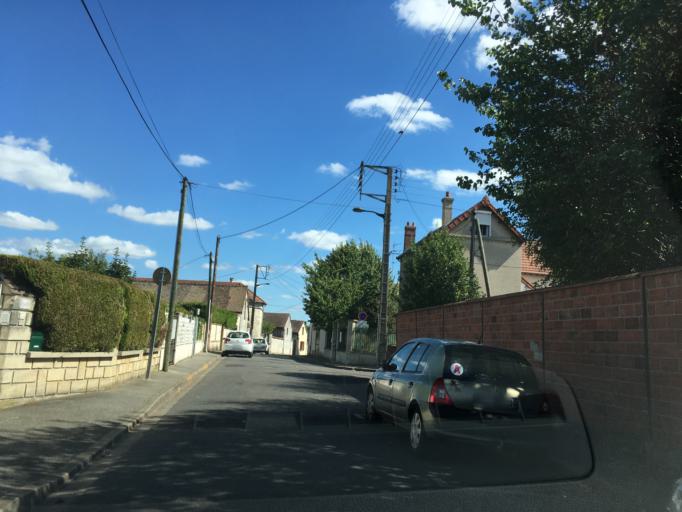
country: FR
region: Haute-Normandie
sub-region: Departement de l'Eure
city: Vernon
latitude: 49.0861
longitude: 1.4912
